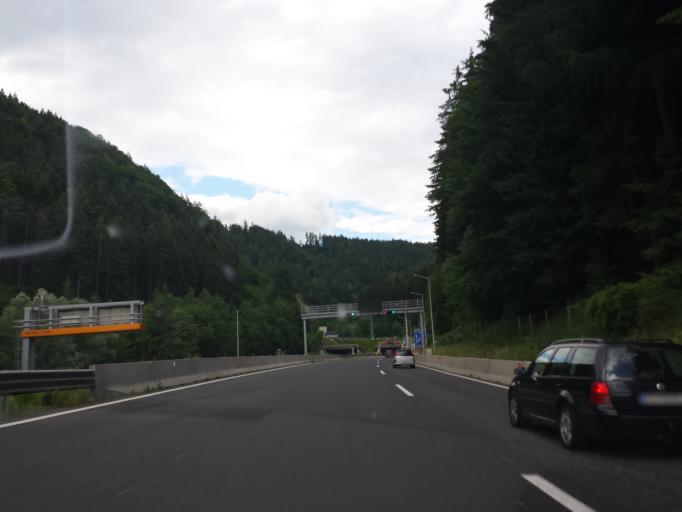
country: AT
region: Styria
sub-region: Politischer Bezirk Bruck-Muerzzuschlag
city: Bruck an der Mur
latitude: 47.4238
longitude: 15.2991
